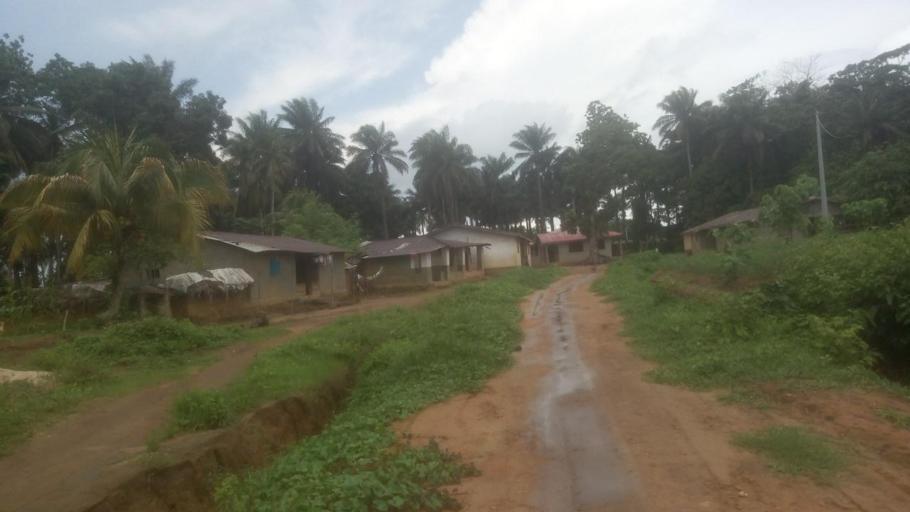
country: SL
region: Northern Province
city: Tintafor
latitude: 8.6389
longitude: -13.2189
